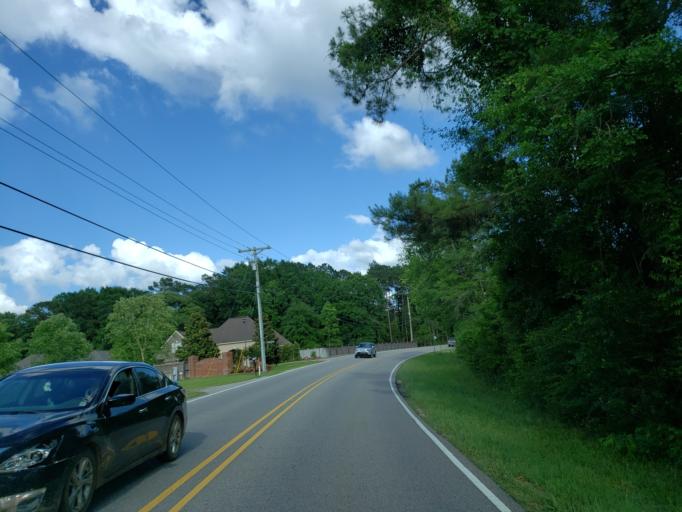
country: US
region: Mississippi
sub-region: Lamar County
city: West Hattiesburg
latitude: 31.2886
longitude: -89.4430
